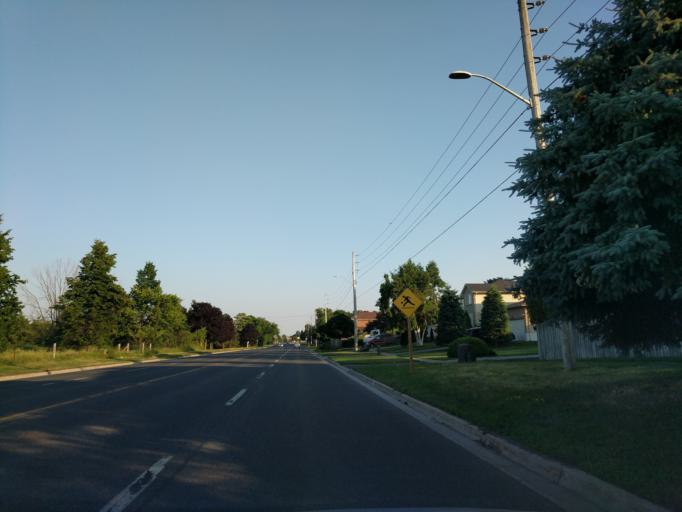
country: CA
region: Ontario
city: Oshawa
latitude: 43.9133
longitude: -78.9027
